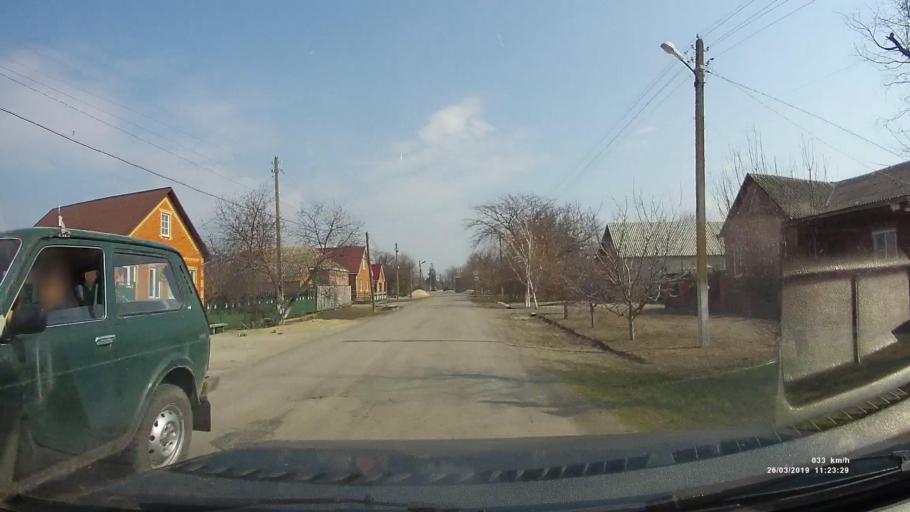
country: RU
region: Rostov
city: Novobessergenovka
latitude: 47.1404
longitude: 38.5602
